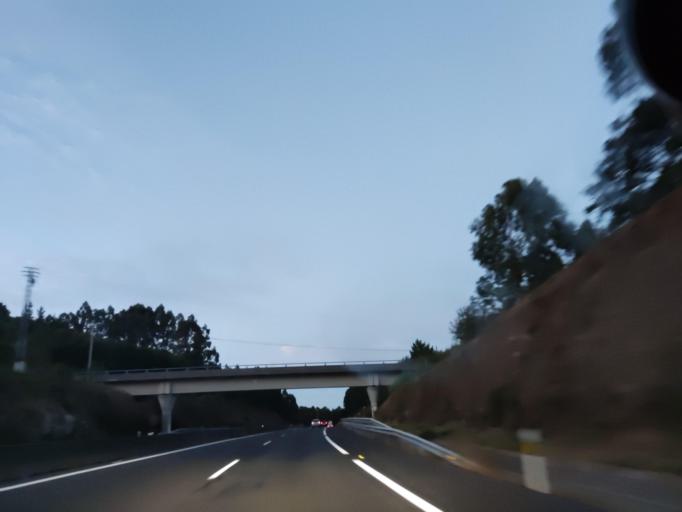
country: ES
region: Galicia
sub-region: Provincia da Coruna
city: Boiro
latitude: 42.6308
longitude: -8.9180
